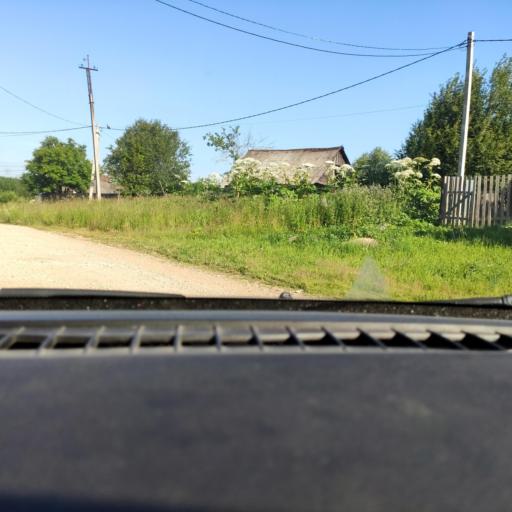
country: RU
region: Perm
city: Perm
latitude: 58.0374
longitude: 56.4013
